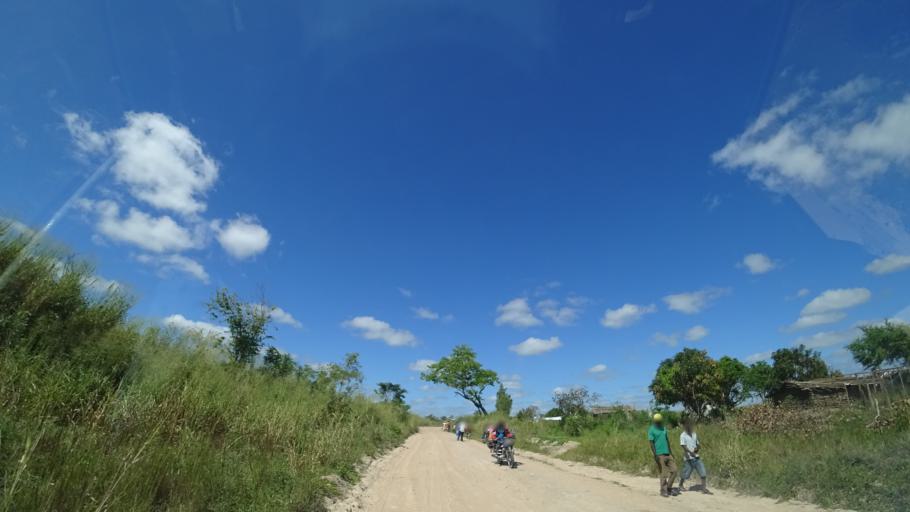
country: MZ
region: Sofala
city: Dondo
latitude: -19.2778
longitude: 34.6822
